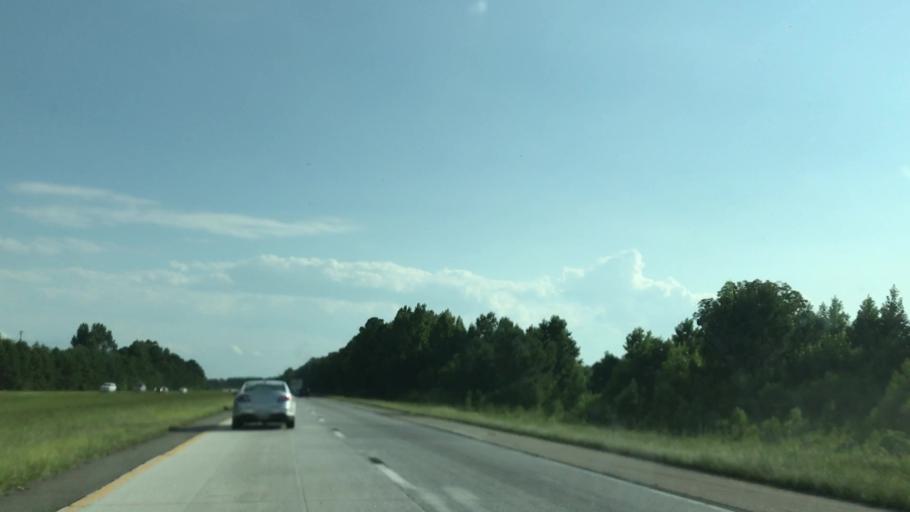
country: US
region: South Carolina
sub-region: Dorchester County
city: Saint George
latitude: 33.1379
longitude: -80.6328
